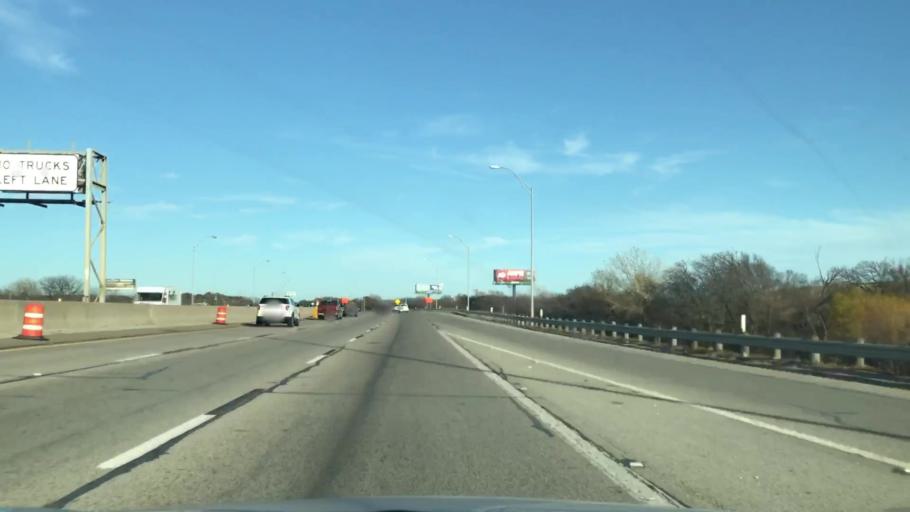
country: US
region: Texas
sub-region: Tarrant County
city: Richland Hills
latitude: 32.7928
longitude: -97.2414
